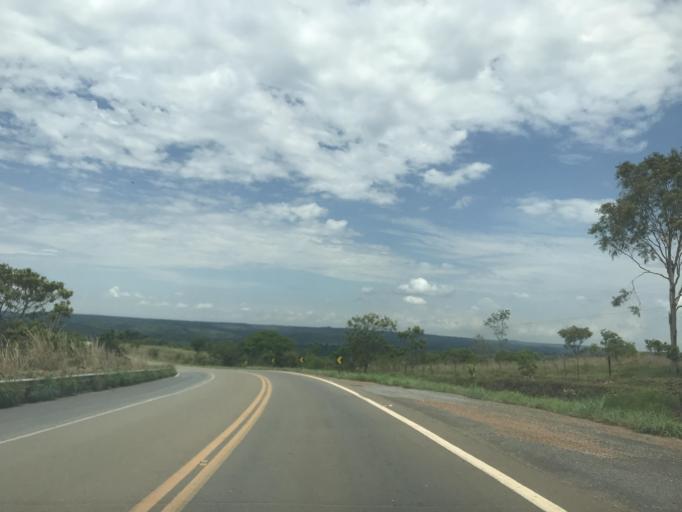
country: BR
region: Goias
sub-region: Luziania
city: Luziania
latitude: -16.3508
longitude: -48.0476
